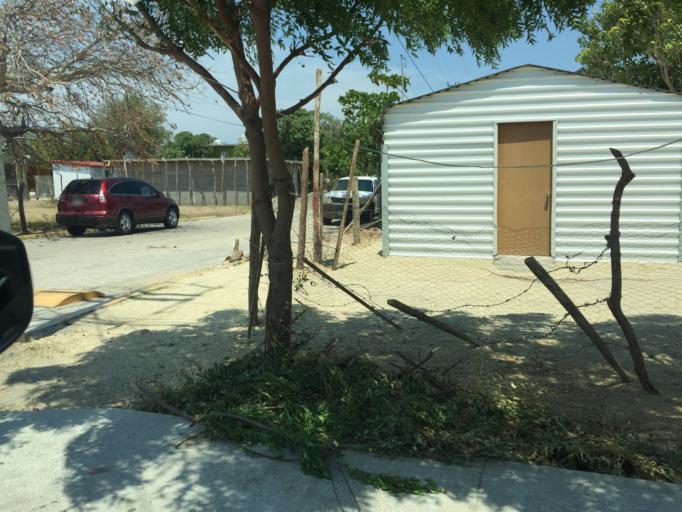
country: MX
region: Oaxaca
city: Asuncion Ixtaltepec
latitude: 16.5067
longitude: -95.0637
